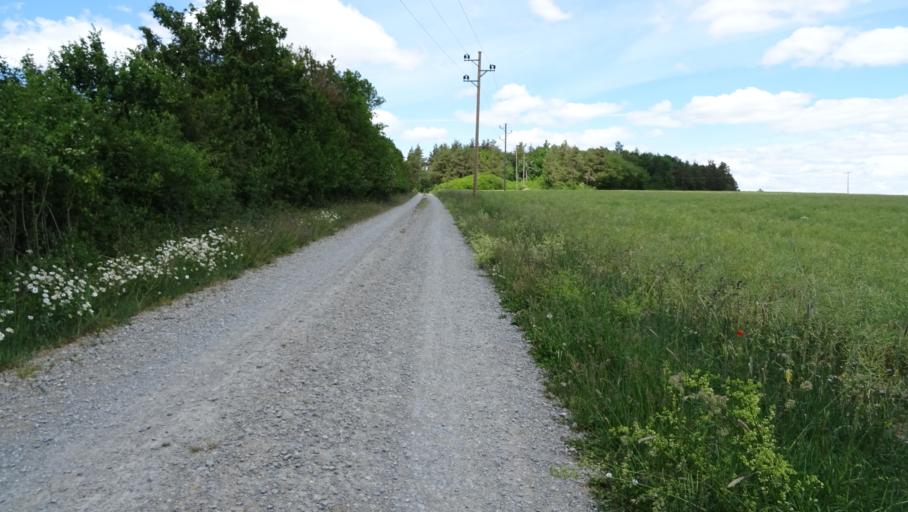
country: DE
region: Baden-Wuerttemberg
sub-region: Karlsruhe Region
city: Seckach
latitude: 49.4708
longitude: 9.3313
